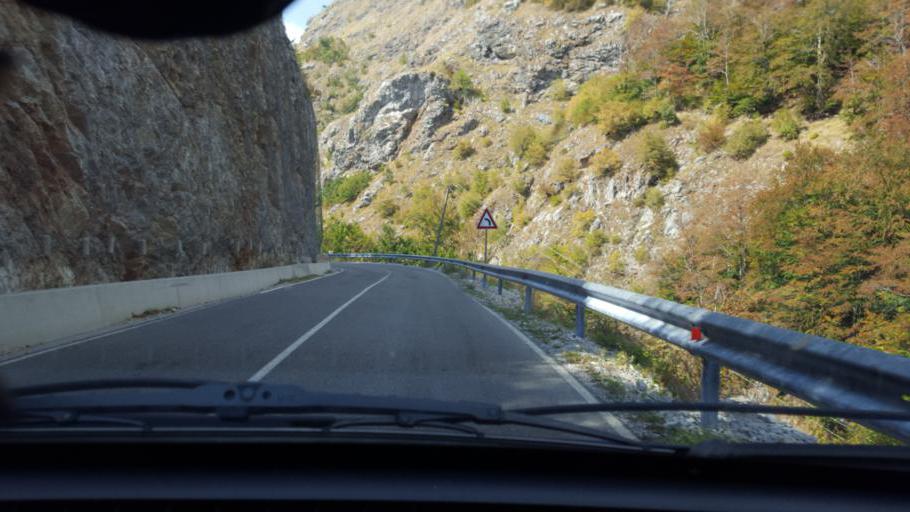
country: AL
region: Kukes
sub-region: Rrethi i Tropojes
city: Valbone
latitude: 42.5369
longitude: 19.6845
